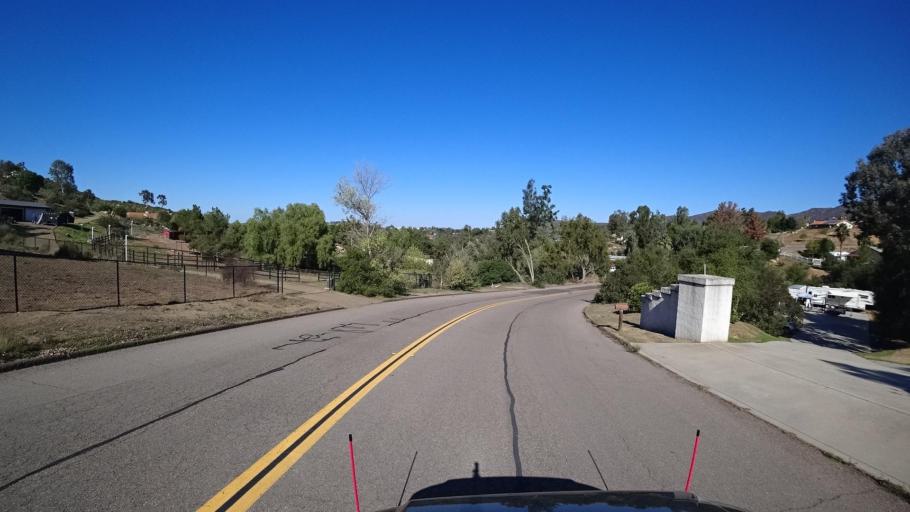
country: US
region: California
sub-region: San Diego County
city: Jamul
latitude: 32.7176
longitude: -116.8496
